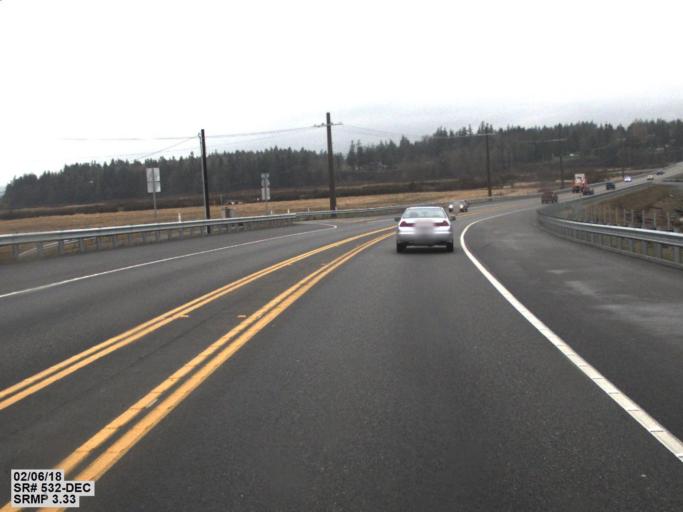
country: US
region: Washington
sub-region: Snohomish County
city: Stanwood
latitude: 48.2400
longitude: -122.3851
